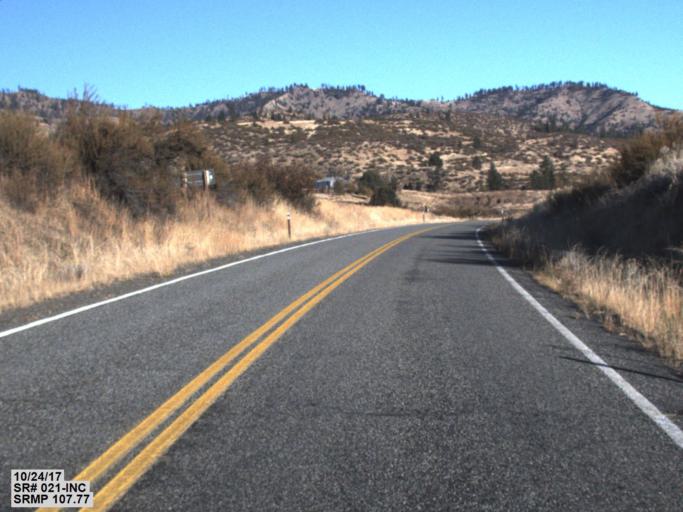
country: US
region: Washington
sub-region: Okanogan County
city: Coulee Dam
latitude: 47.9608
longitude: -118.6999
